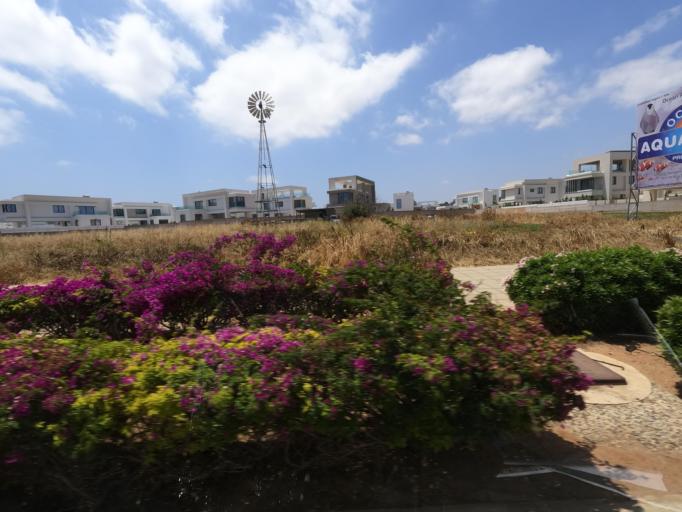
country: CY
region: Ammochostos
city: Protaras
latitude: 35.0351
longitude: 34.0257
